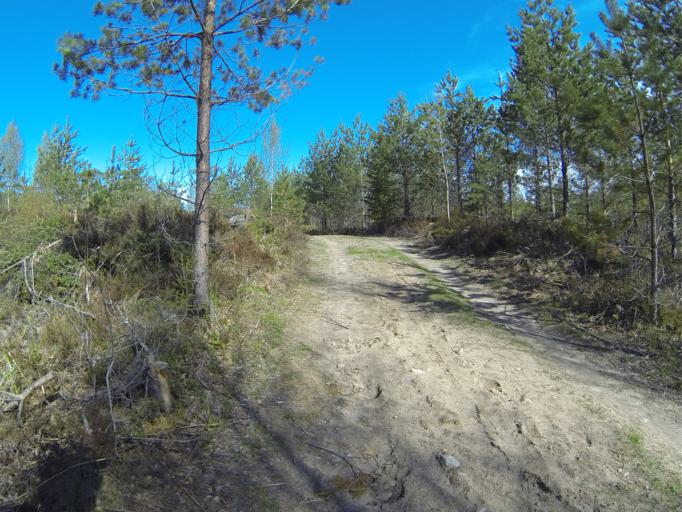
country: FI
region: Varsinais-Suomi
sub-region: Salo
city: Pertteli
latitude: 60.3984
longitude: 23.2118
